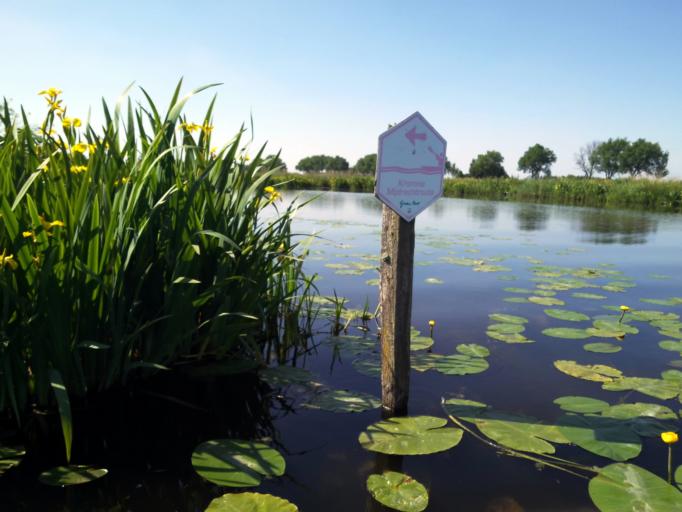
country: NL
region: Utrecht
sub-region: Gemeente De Ronde Venen
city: Mijdrecht
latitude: 52.1791
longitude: 4.8747
